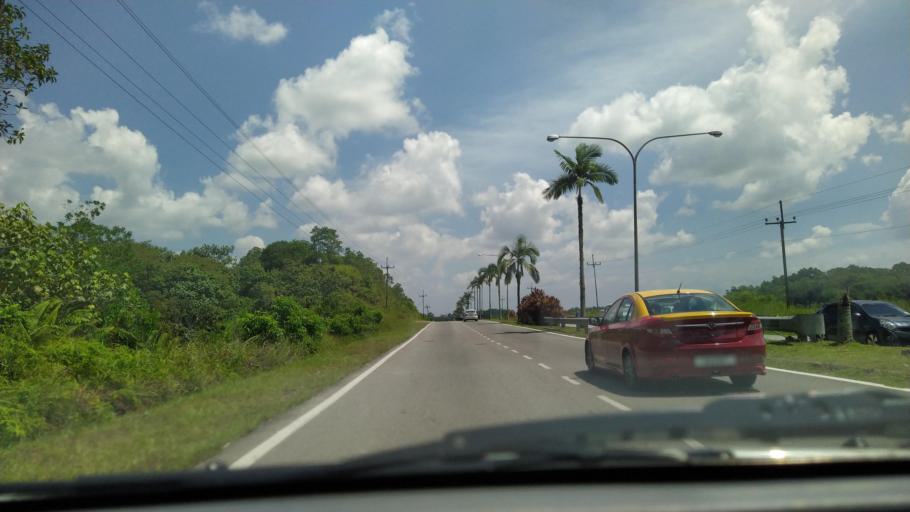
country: MY
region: Sarawak
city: Sibu
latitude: 2.2877
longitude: 111.9512
